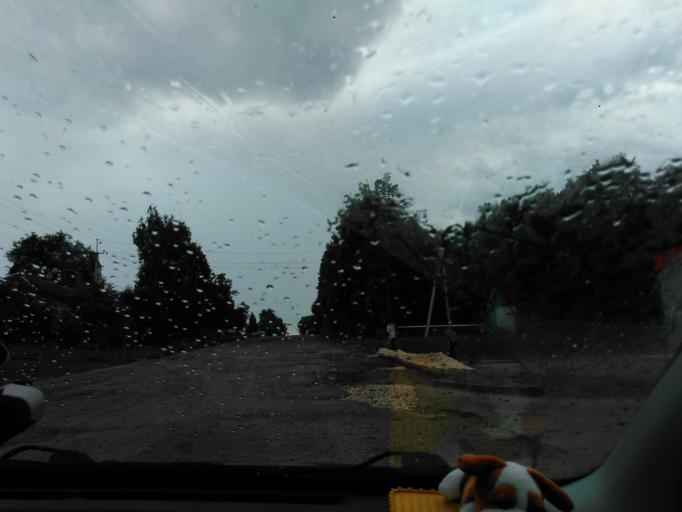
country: RU
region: Penza
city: Belinskiy
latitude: 52.9693
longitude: 43.4220
